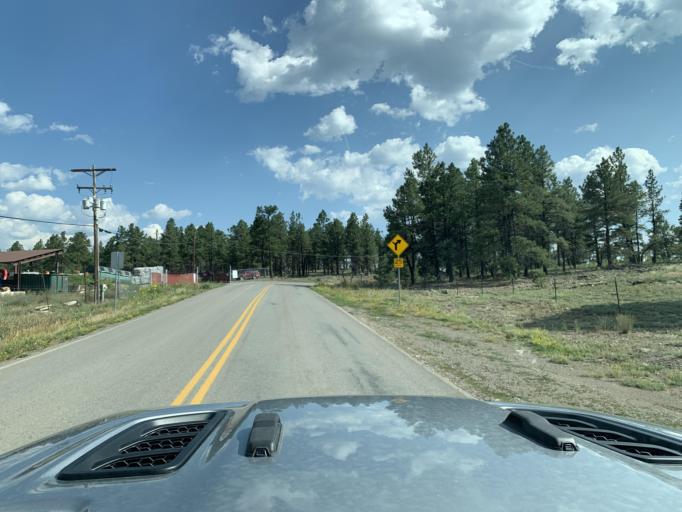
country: US
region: Colorado
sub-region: Archuleta County
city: Pagosa Springs
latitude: 37.2413
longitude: -107.0254
